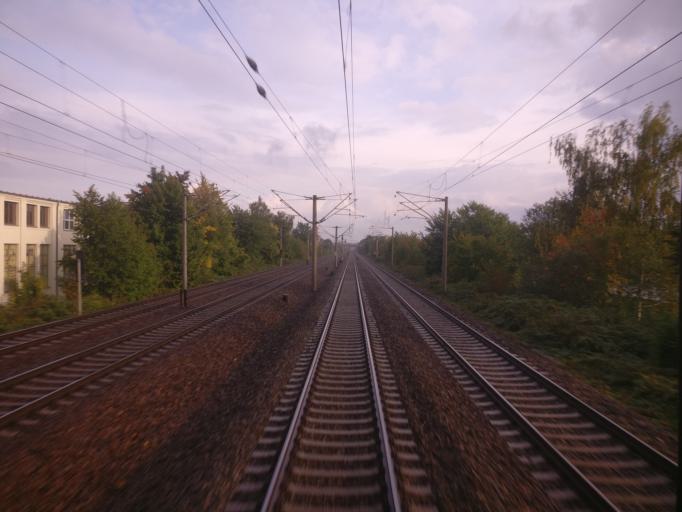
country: DE
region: Saxony
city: Heidenau
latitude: 51.0090
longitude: 13.8129
